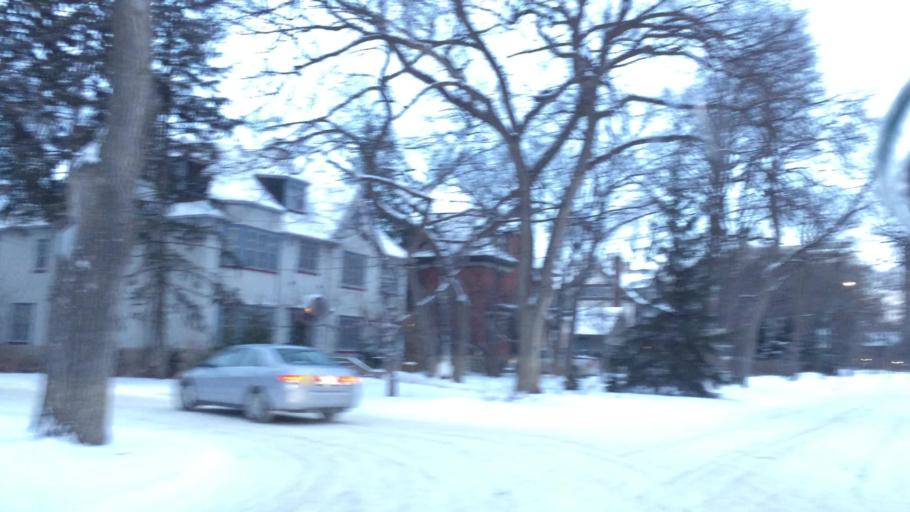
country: CA
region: Manitoba
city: Winnipeg
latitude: 49.8764
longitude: -97.1576
